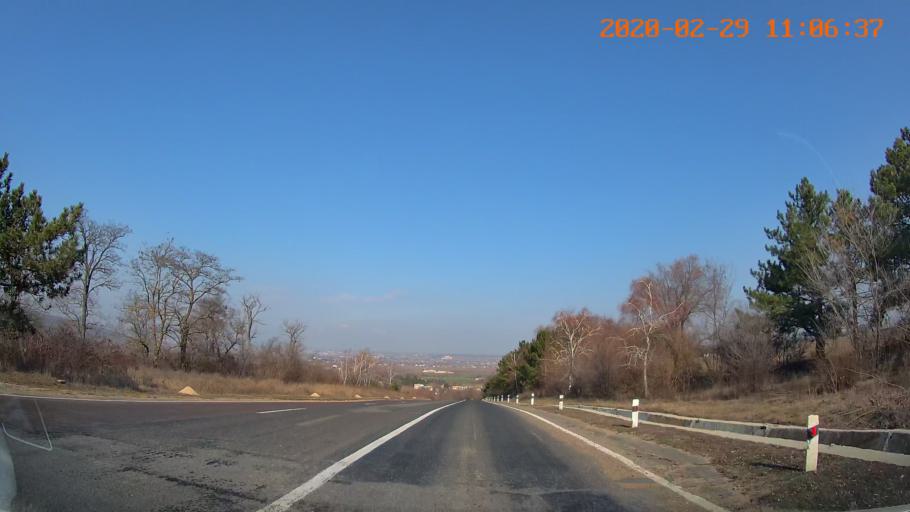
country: MD
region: Criuleni
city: Criuleni
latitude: 47.2166
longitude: 29.1871
